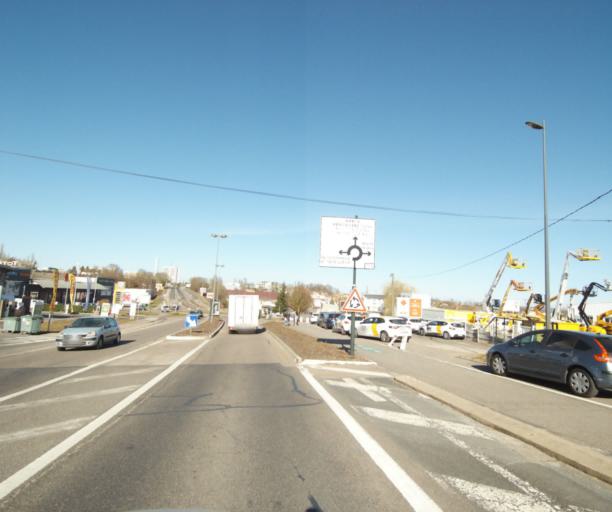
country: FR
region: Lorraine
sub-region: Departement de Meurthe-et-Moselle
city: Vandoeuvre-les-Nancy
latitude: 48.6543
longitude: 6.1858
